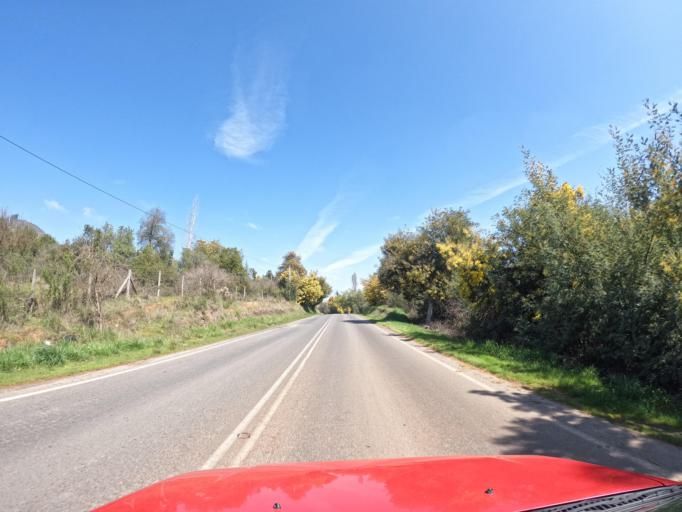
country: CL
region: Maule
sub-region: Provincia de Talca
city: San Clemente
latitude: -35.4812
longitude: -71.2699
